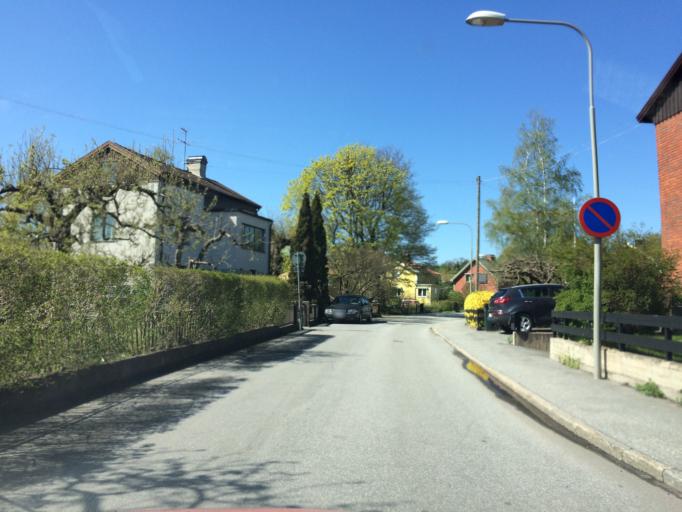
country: SE
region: Stockholm
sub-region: Huddinge Kommun
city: Segeltorp
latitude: 59.2909
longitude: 17.9555
